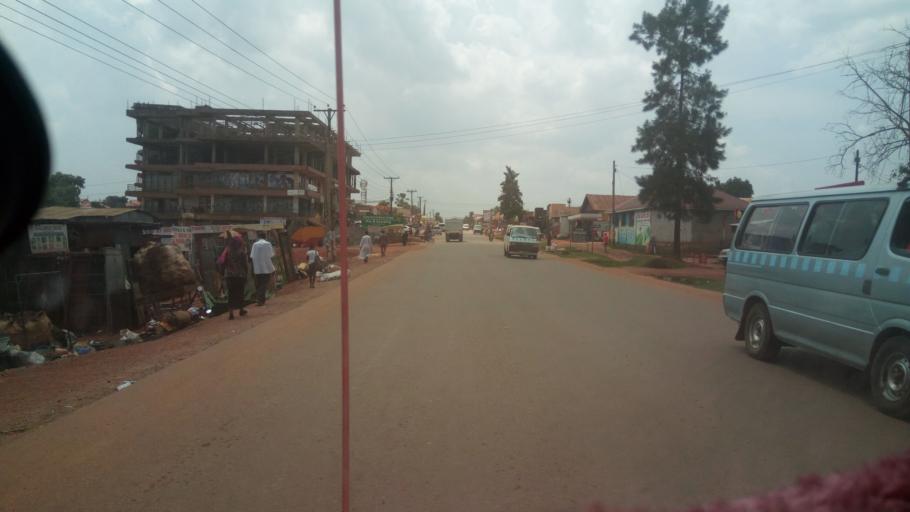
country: UG
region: Central Region
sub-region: Wakiso District
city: Wakiso
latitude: 0.3757
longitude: 32.5207
